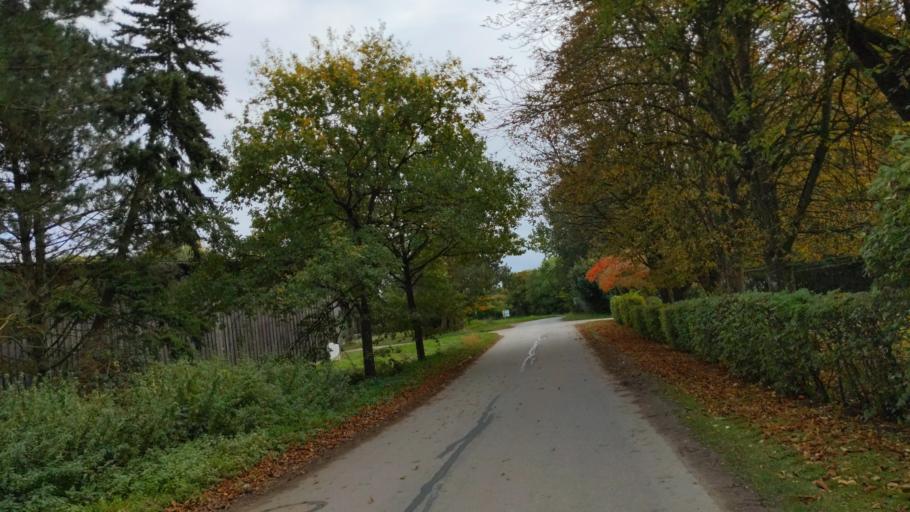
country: DE
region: Schleswig-Holstein
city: Sierksdorf
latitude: 54.0886
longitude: 10.7452
